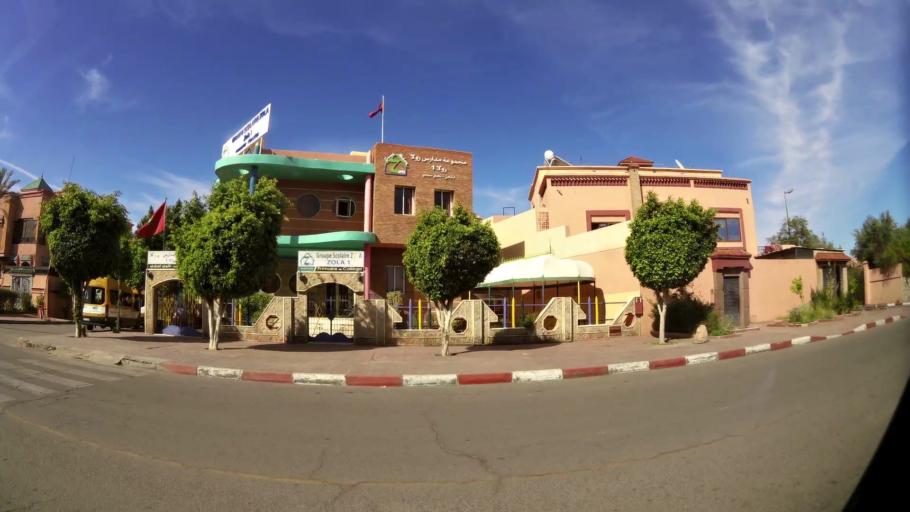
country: MA
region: Marrakech-Tensift-Al Haouz
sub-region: Marrakech
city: Marrakesh
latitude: 31.6553
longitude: -8.0110
